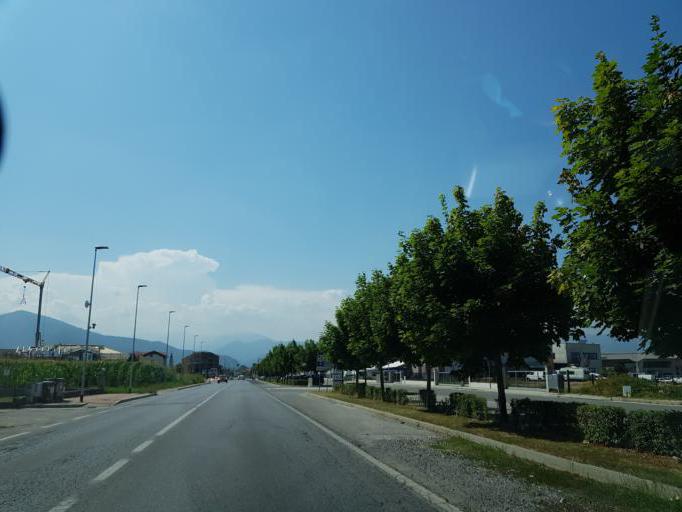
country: IT
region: Piedmont
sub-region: Provincia di Cuneo
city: San Rocco
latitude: 44.3970
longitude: 7.4815
